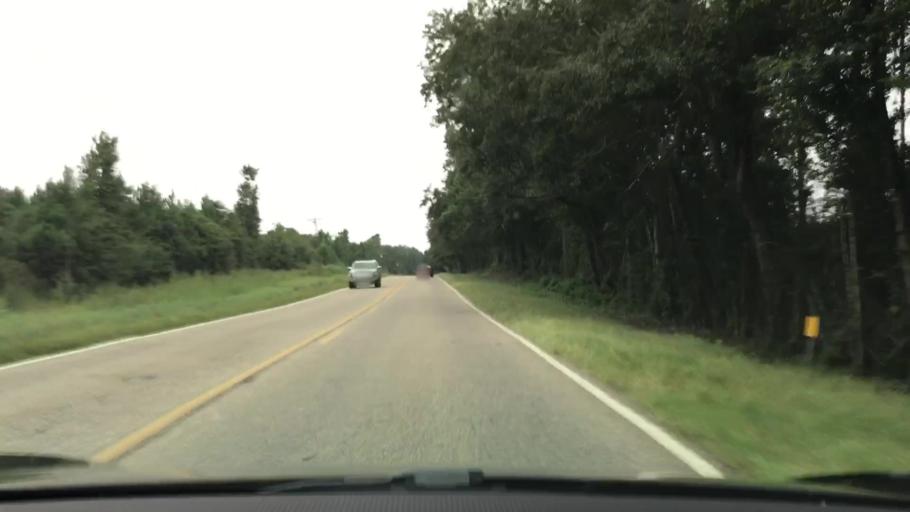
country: US
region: Alabama
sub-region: Geneva County
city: Samson
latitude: 31.1365
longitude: -86.1355
